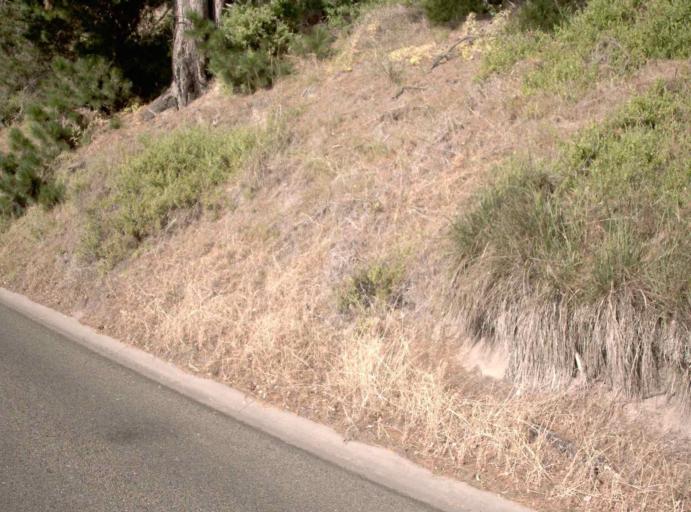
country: AU
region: Victoria
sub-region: East Gippsland
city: Lakes Entrance
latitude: -37.8859
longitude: 147.8595
